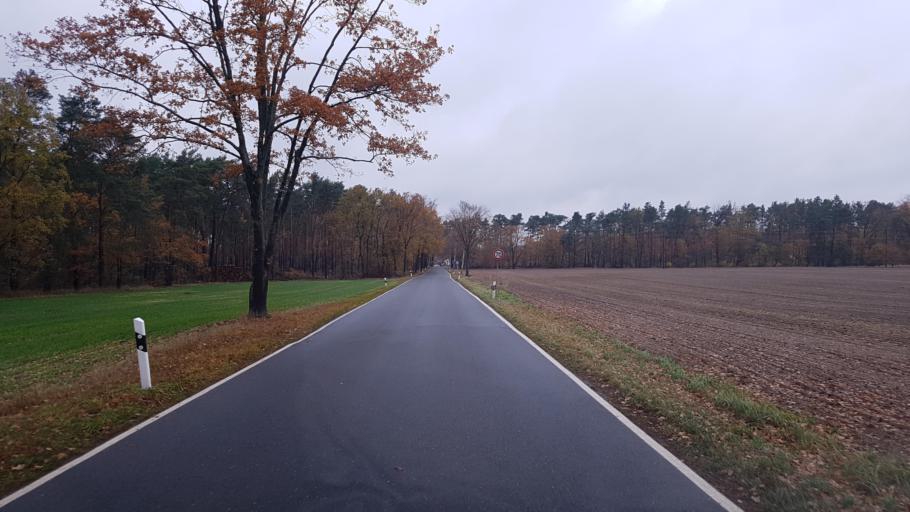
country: DE
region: Brandenburg
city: Drebkau
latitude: 51.6910
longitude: 14.1992
